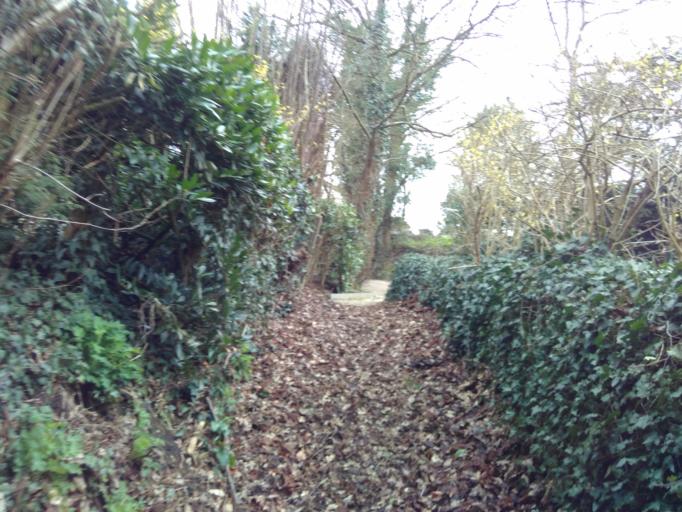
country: BE
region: Wallonia
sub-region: Province du Brabant Wallon
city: Chaumont-Gistoux
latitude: 50.6779
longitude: 4.7219
